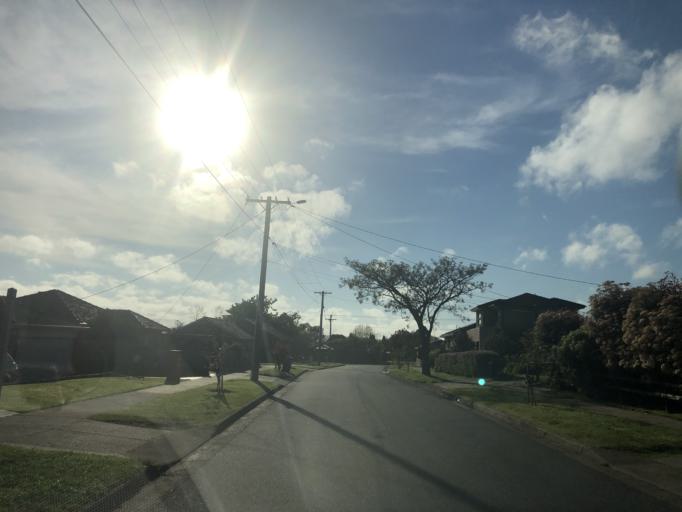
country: AU
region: Victoria
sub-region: Casey
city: Eumemmerring
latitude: -37.9994
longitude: 145.2554
